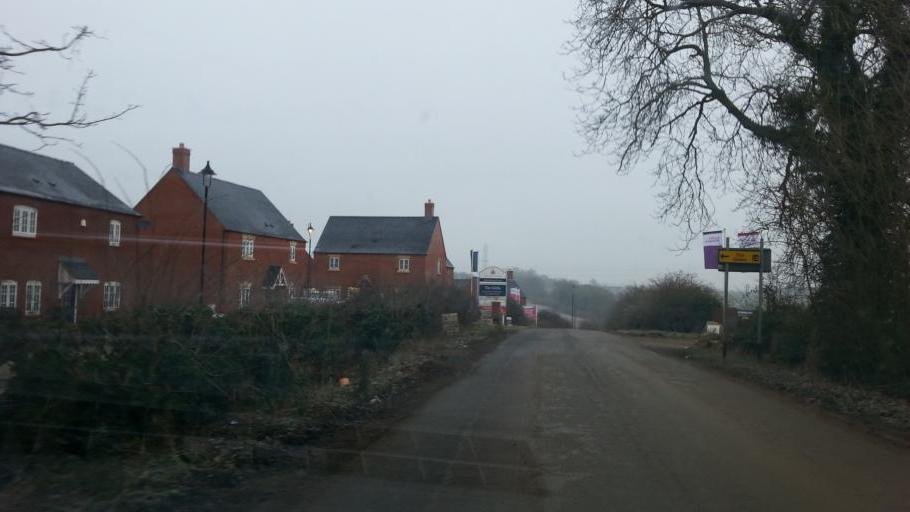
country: GB
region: England
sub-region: Northamptonshire
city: Brackley
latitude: 52.0438
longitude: -1.1448
